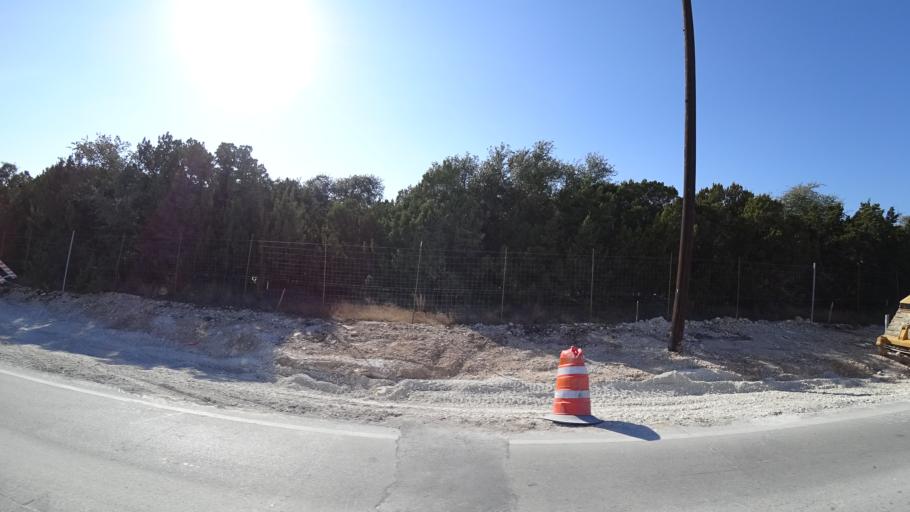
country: US
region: Texas
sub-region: Williamson County
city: Cedar Park
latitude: 30.4974
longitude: -97.8571
